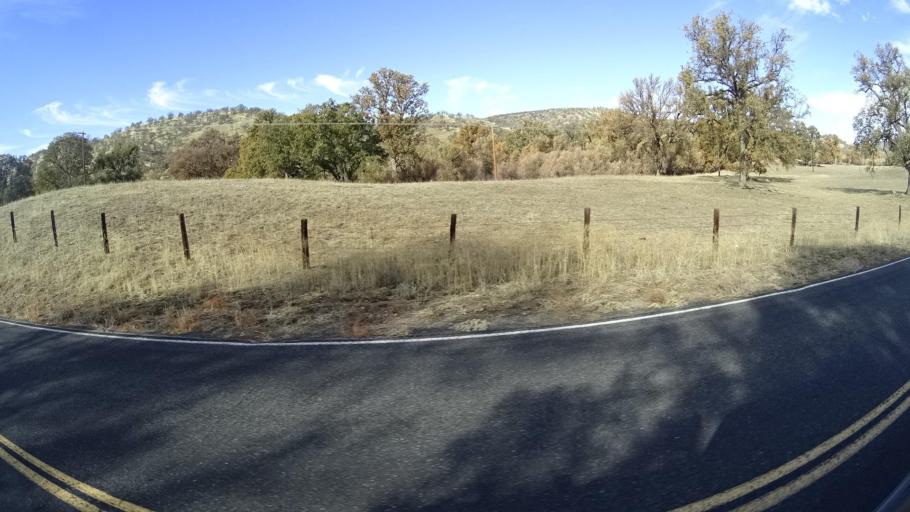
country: US
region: California
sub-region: Kern County
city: Alta Sierra
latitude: 35.6756
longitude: -118.7343
